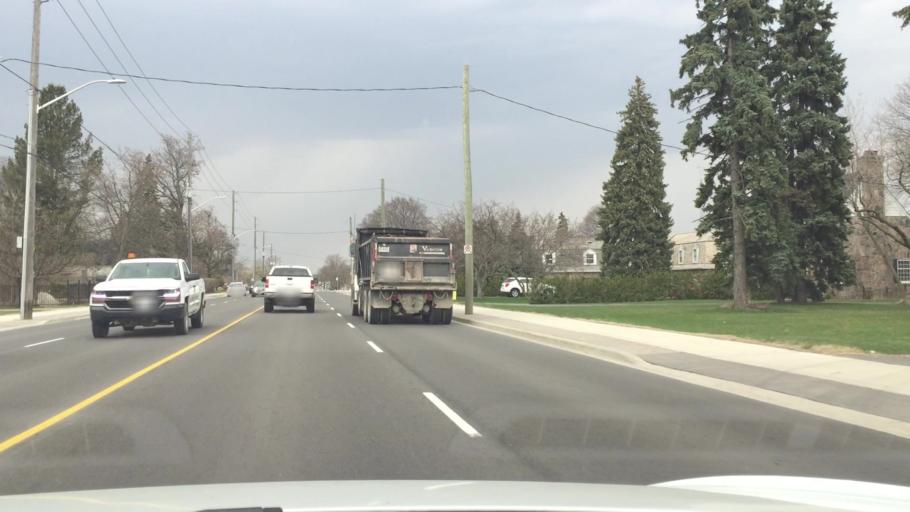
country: CA
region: Ontario
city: Oshawa
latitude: 43.9172
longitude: -78.8720
